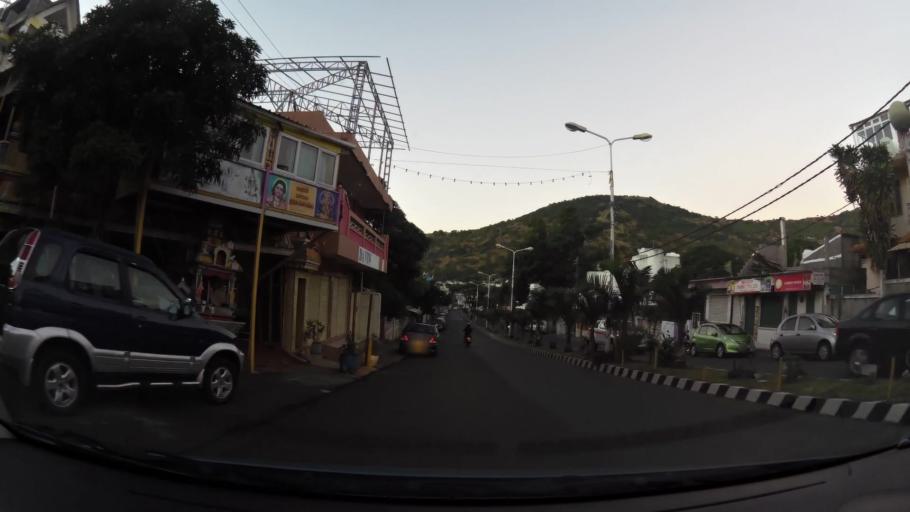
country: MU
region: Port Louis
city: Port Louis
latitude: -20.1678
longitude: 57.5151
